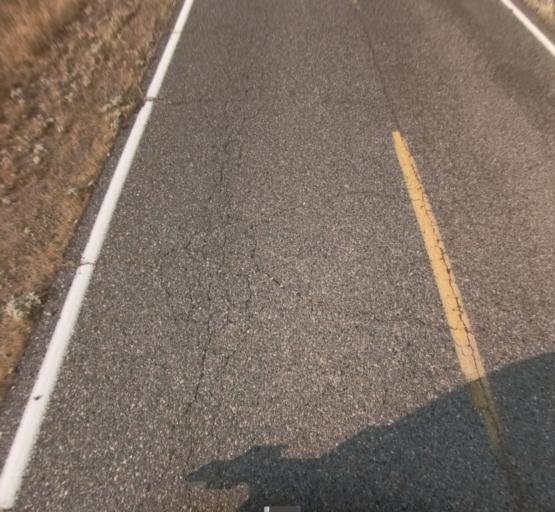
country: US
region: California
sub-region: Madera County
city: Madera Acres
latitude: 37.1566
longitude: -120.0028
